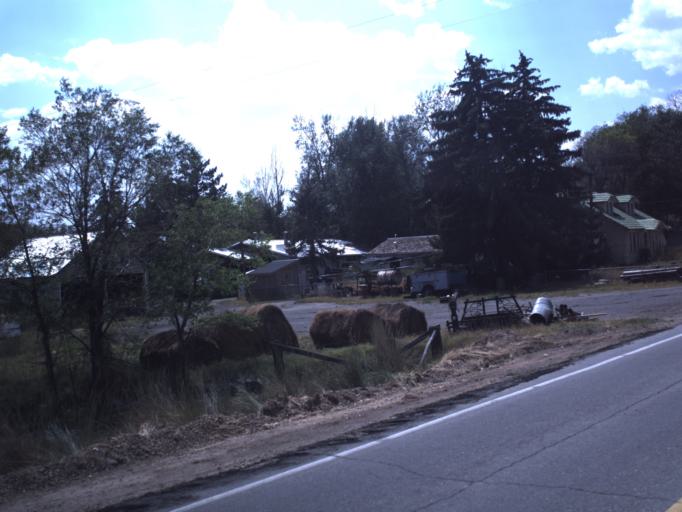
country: US
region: Utah
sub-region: Duchesne County
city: Roosevelt
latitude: 40.4330
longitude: -110.0282
